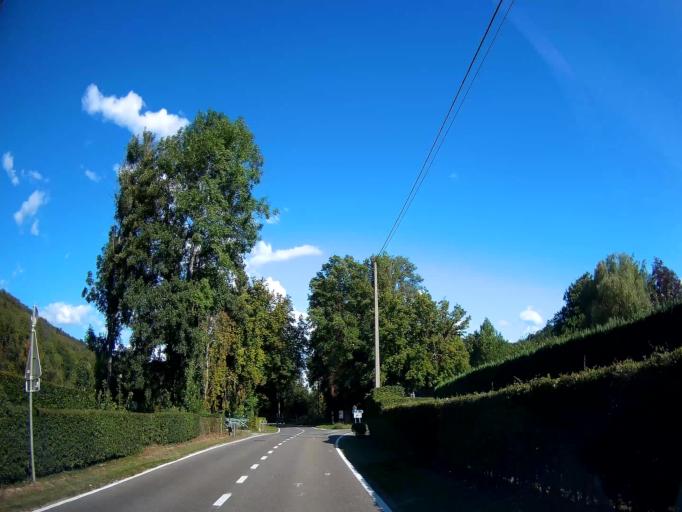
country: BE
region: Wallonia
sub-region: Province de Namur
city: Anhee
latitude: 50.3171
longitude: 4.8618
